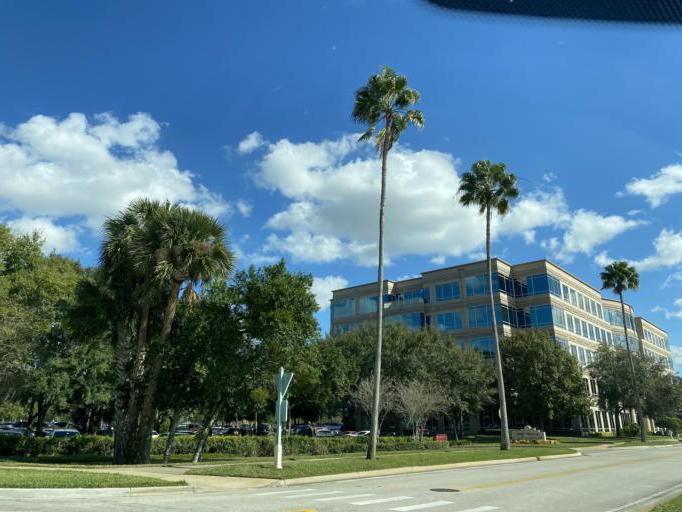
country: US
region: Florida
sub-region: Seminole County
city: Heathrow
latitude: 28.7899
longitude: -81.3542
